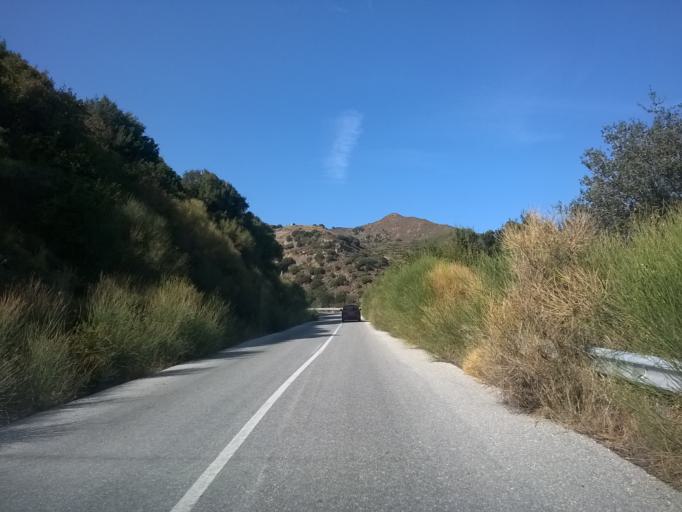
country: GR
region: South Aegean
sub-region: Nomos Kykladon
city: Filotion
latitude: 37.1418
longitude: 25.5382
